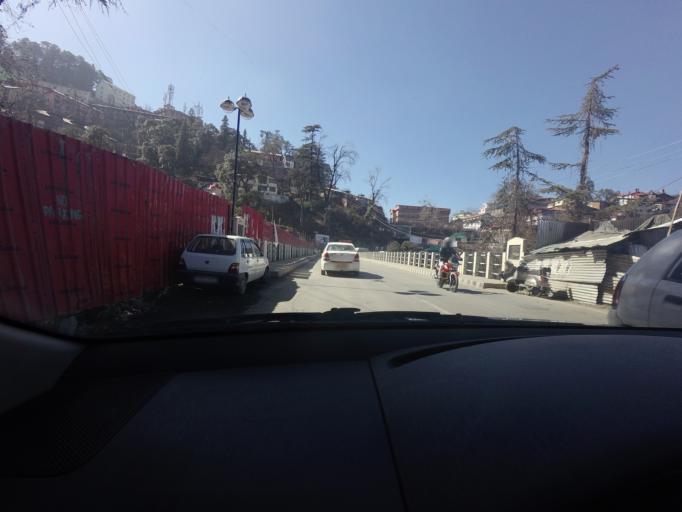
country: IN
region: Himachal Pradesh
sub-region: Shimla
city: Shimla
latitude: 31.1081
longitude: 77.1810
